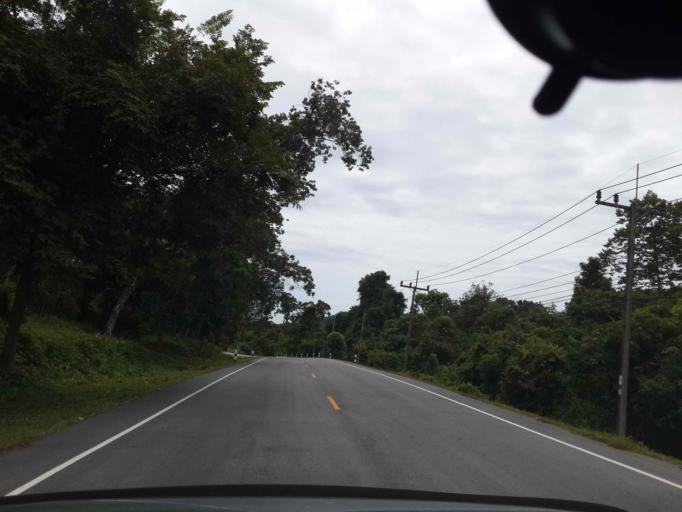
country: TH
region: Narathiwat
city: Rueso
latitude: 6.3605
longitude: 101.5882
